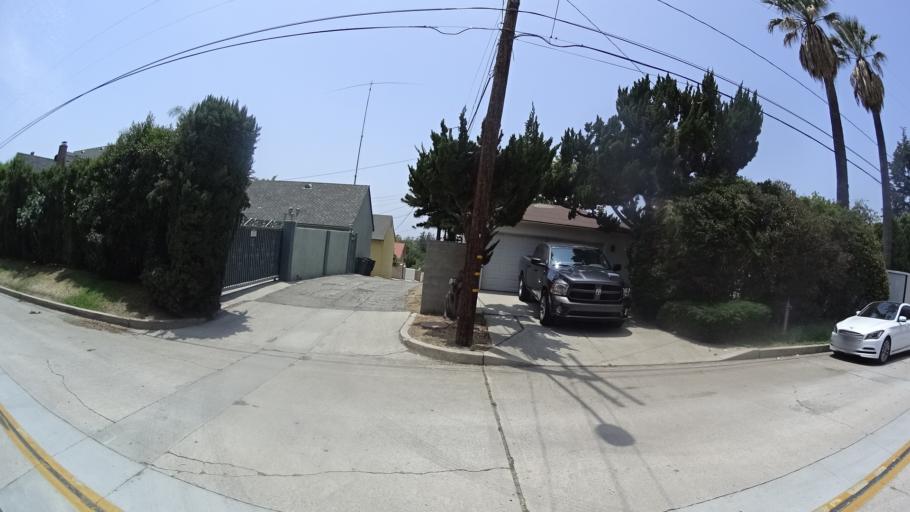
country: US
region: California
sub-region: Los Angeles County
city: Burbank
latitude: 34.1957
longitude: -118.3009
